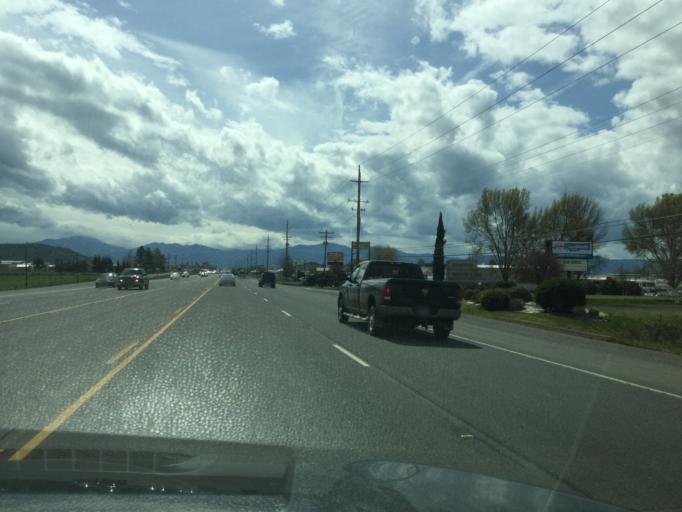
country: US
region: Oregon
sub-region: Jackson County
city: White City
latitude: 42.4076
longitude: -122.8562
